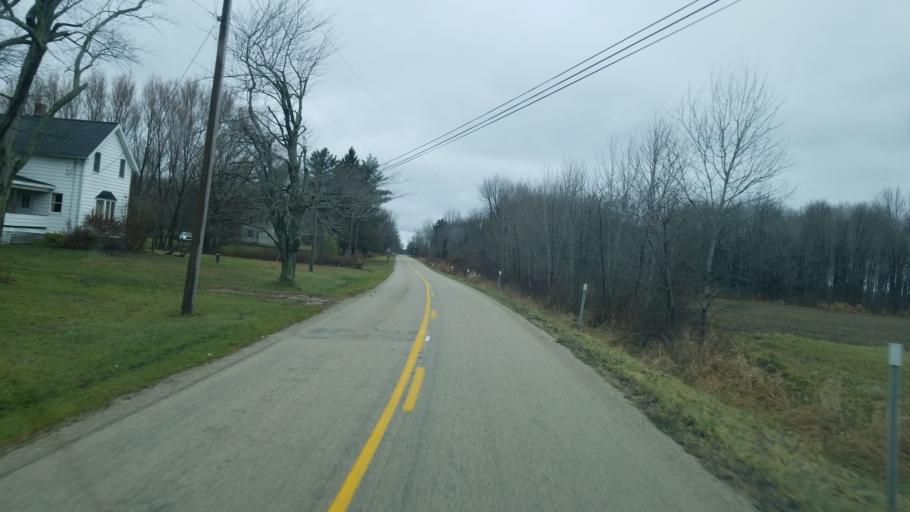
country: US
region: Ohio
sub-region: Ashtabula County
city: Andover
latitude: 41.6924
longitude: -80.6130
